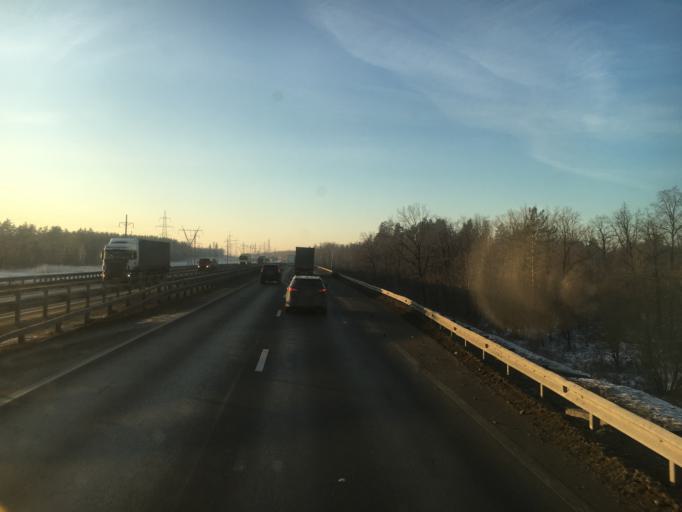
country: RU
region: Samara
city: Pribrezhnyy
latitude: 53.5178
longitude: 49.8346
